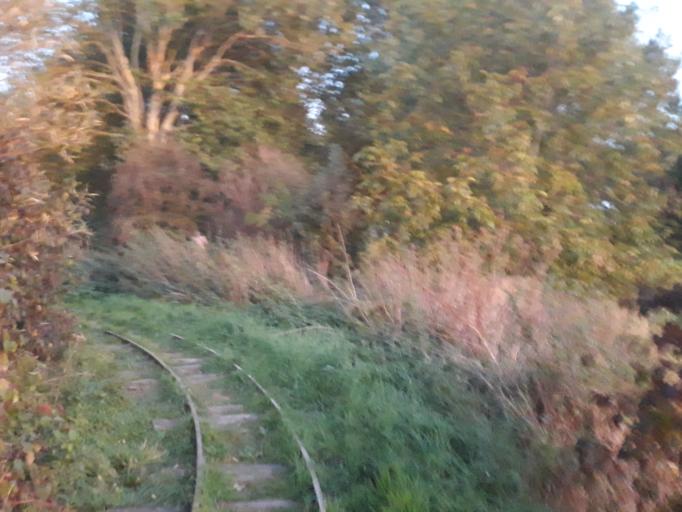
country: NL
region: Gelderland
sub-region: Gemeente Zevenaar
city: Zevenaar
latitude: 51.9165
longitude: 6.0722
